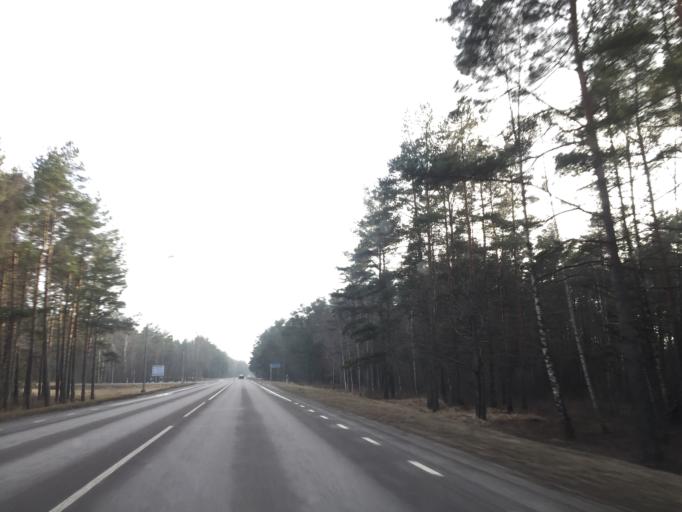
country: EE
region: Saare
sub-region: Kuressaare linn
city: Kuressaare
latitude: 58.4118
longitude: 22.7794
